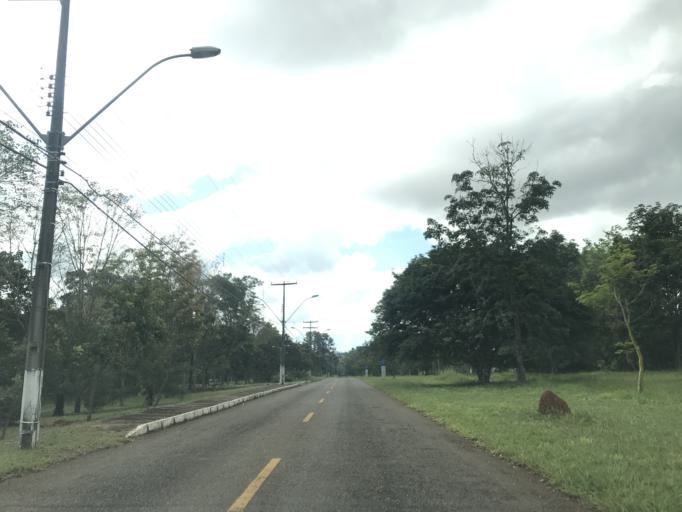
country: BR
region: Federal District
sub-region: Brasilia
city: Brasilia
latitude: -15.8923
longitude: -47.9252
